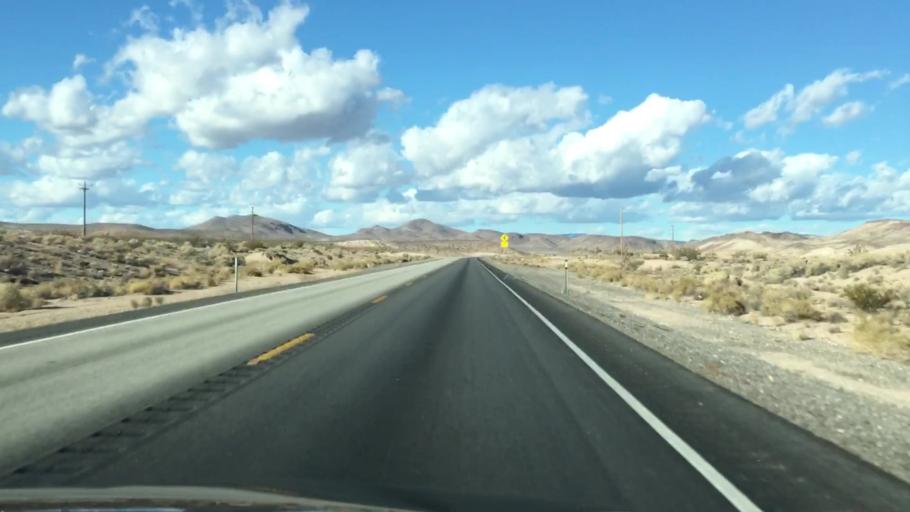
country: US
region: Nevada
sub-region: Nye County
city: Beatty
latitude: 36.9866
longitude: -116.7247
